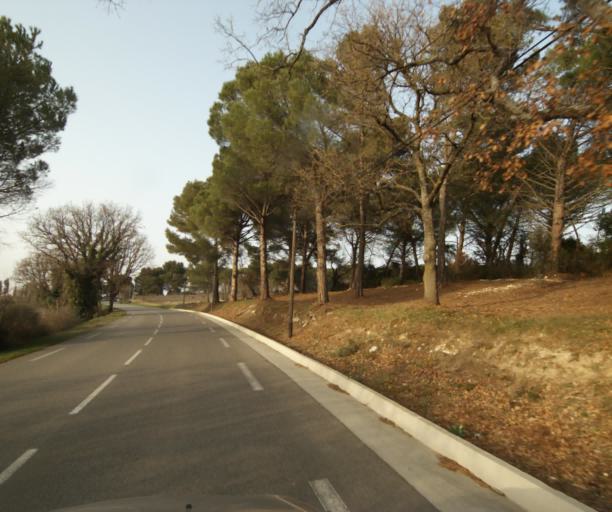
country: FR
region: Provence-Alpes-Cote d'Azur
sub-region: Departement des Bouches-du-Rhone
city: Eguilles
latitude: 43.5914
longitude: 5.3674
